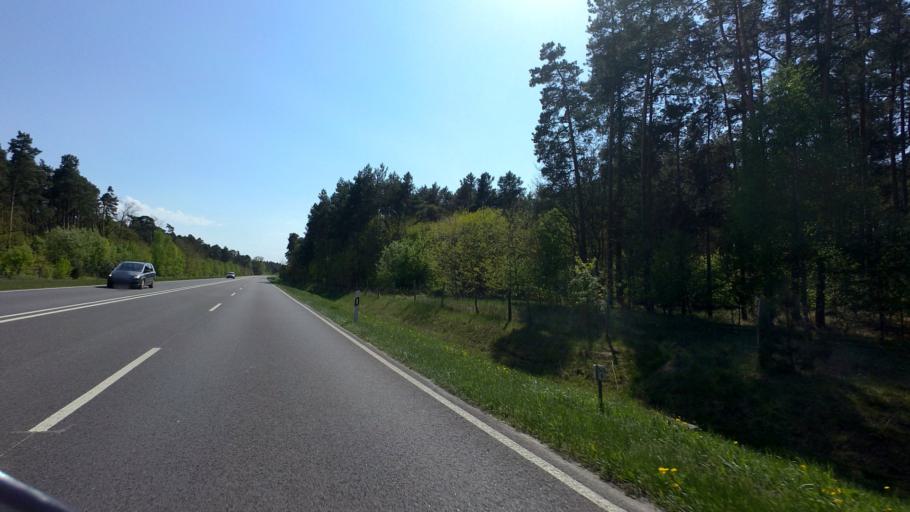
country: DE
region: Brandenburg
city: Beeskow
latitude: 52.1597
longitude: 14.2168
